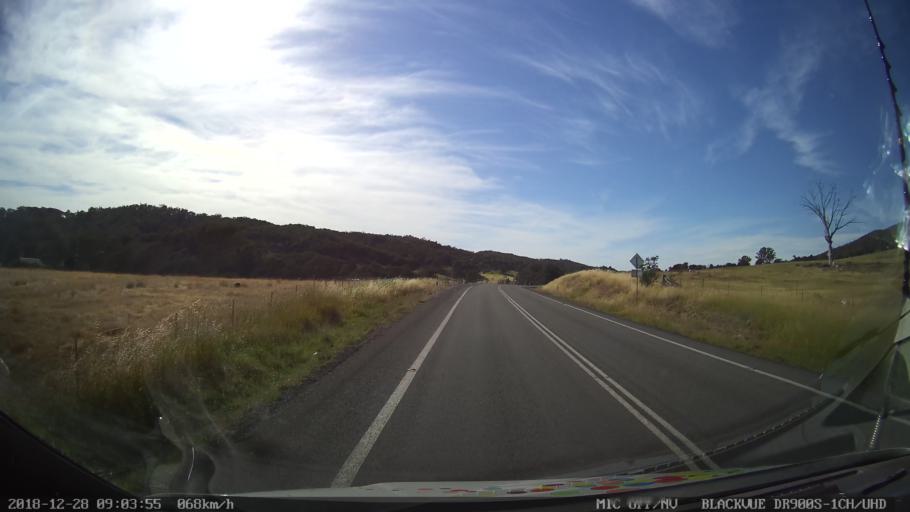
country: AU
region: New South Wales
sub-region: Upper Lachlan Shire
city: Crookwell
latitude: -34.1677
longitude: 149.3403
